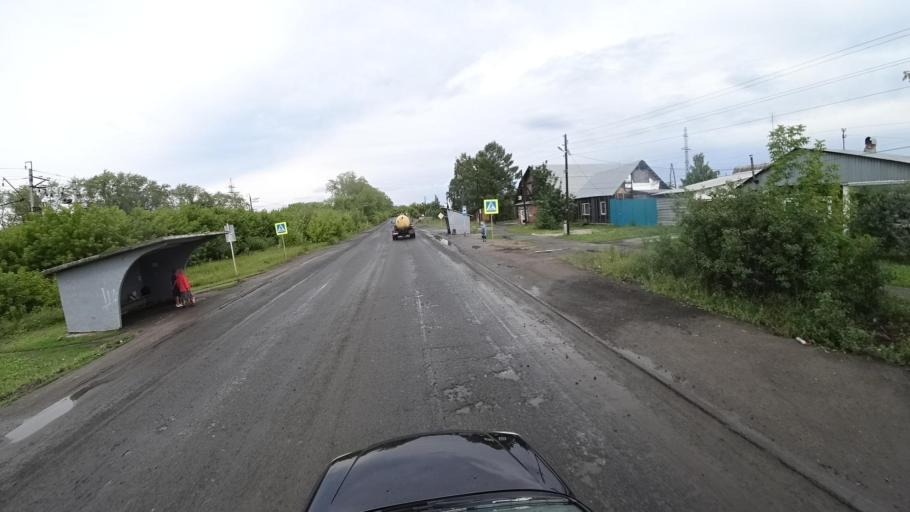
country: RU
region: Sverdlovsk
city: Kamyshlov
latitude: 56.8448
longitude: 62.7493
